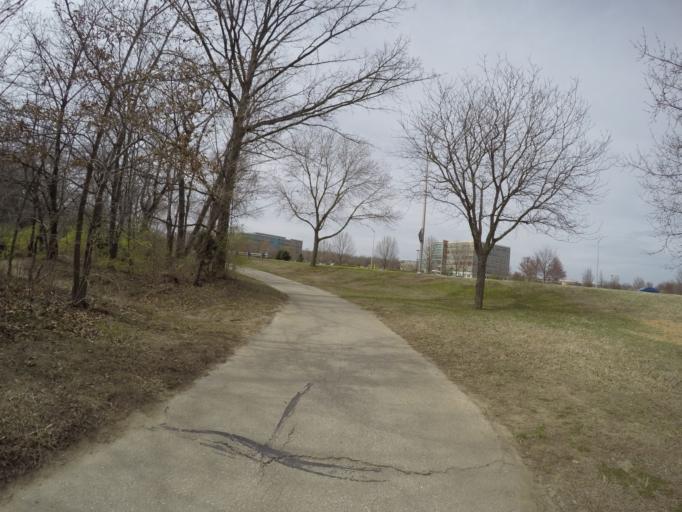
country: US
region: Kansas
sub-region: Johnson County
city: Leawood
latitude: 38.9201
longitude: -94.6281
